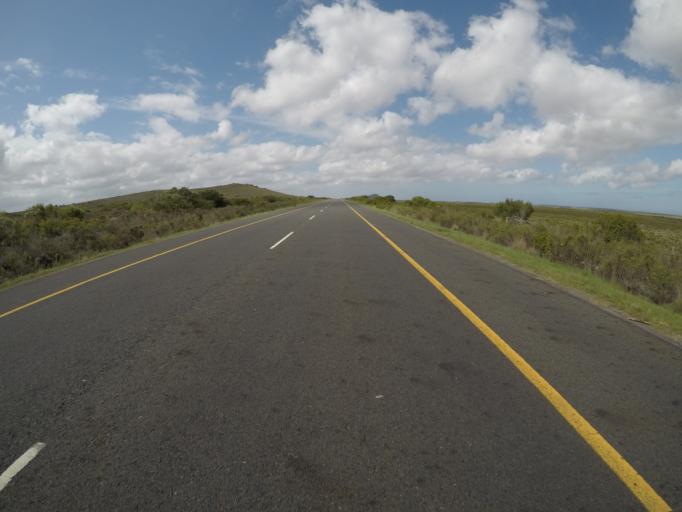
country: ZA
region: Western Cape
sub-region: Eden District Municipality
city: Mossel Bay
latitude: -34.1910
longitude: 21.8398
